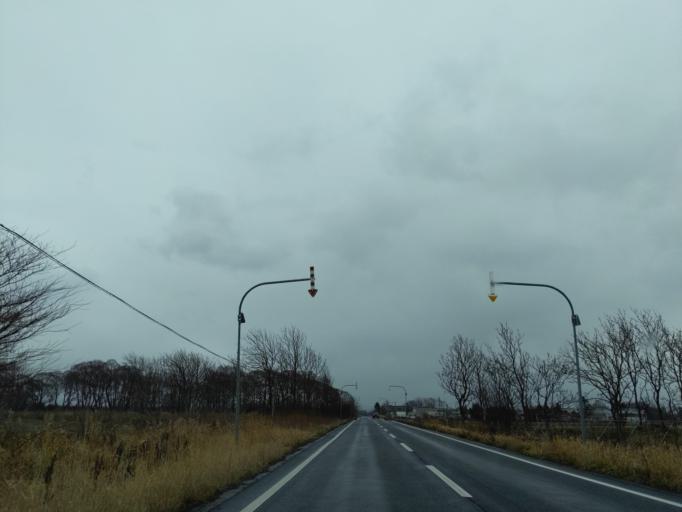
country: JP
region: Hokkaido
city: Ebetsu
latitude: 43.1004
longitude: 141.6093
